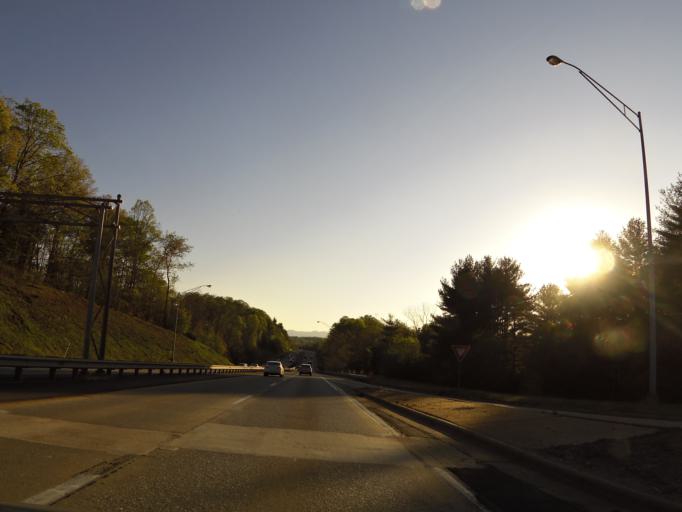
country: US
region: North Carolina
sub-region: Buncombe County
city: Asheville
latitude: 35.5636
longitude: -82.5952
